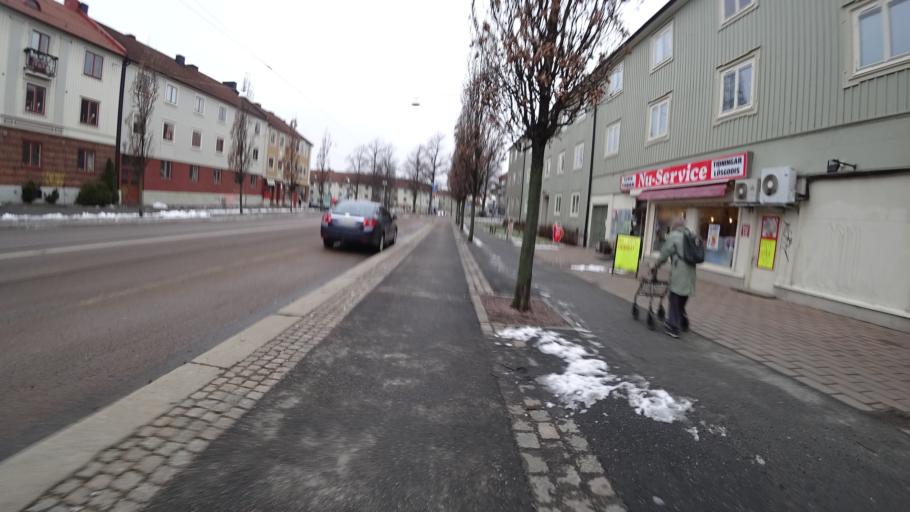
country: SE
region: Vaestra Goetaland
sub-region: Goteborg
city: Majorna
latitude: 57.6864
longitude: 11.9229
